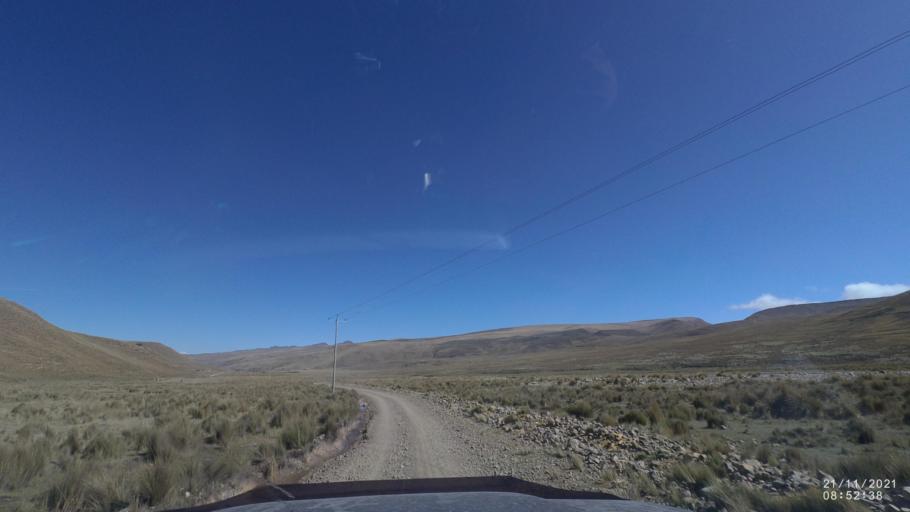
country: BO
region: Cochabamba
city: Cochabamba
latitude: -17.2125
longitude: -66.2392
